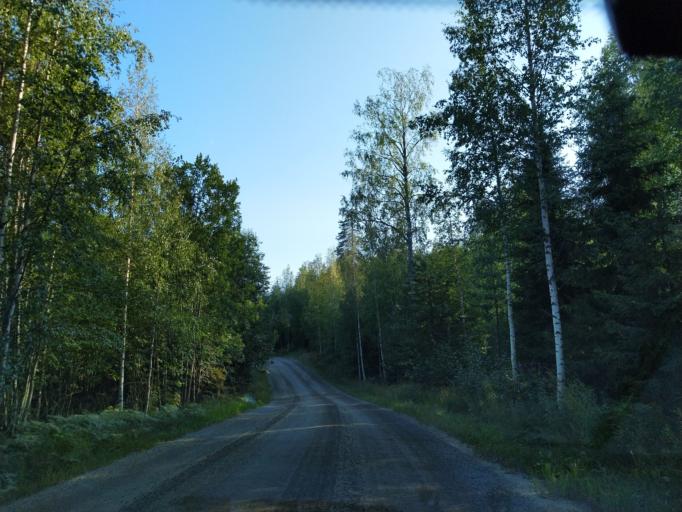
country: FI
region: Central Finland
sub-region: Jaemsae
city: Kuhmoinen
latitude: 61.6331
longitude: 25.0928
